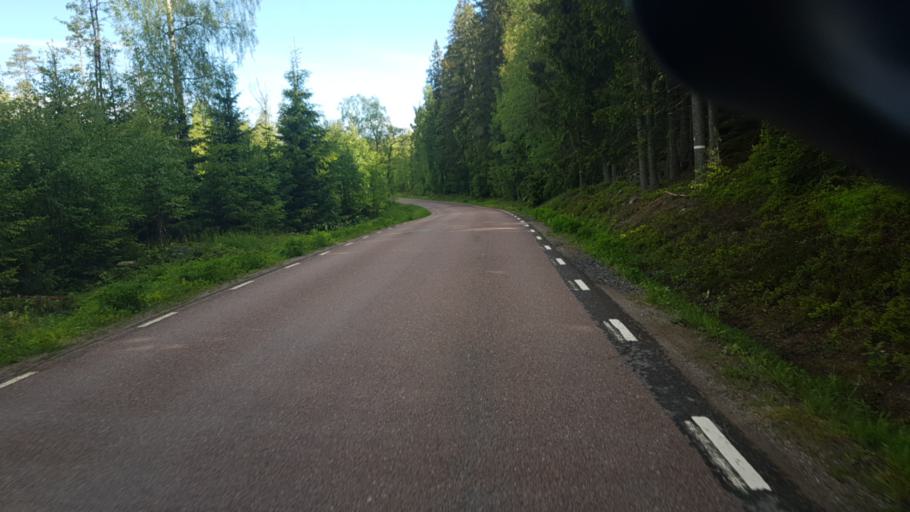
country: NO
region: Hedmark
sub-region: Eidskog
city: Skotterud
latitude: 59.8076
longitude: 12.0311
